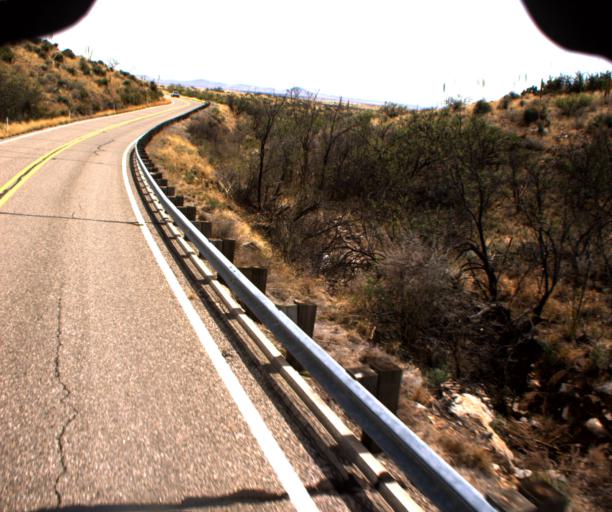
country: US
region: Arizona
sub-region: Cochise County
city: Willcox
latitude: 32.1517
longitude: -109.5648
